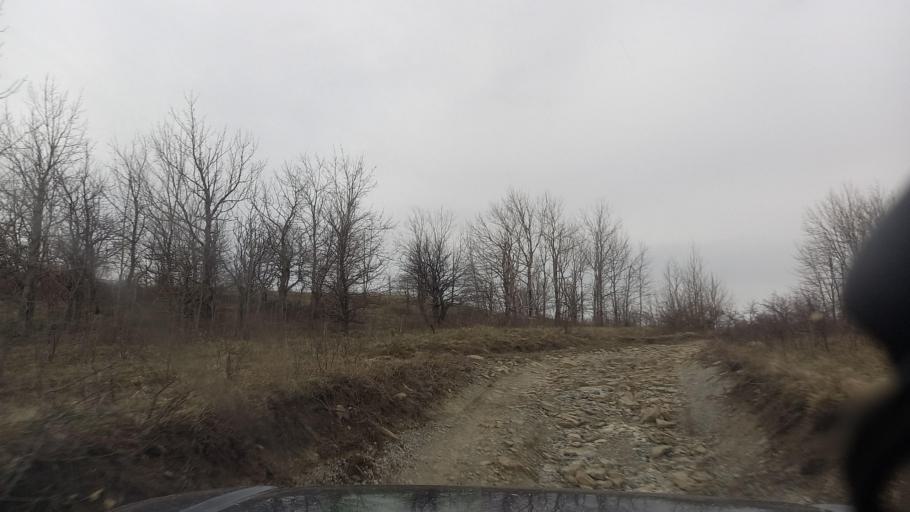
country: RU
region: Krasnodarskiy
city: Pshada
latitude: 44.5967
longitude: 38.2848
